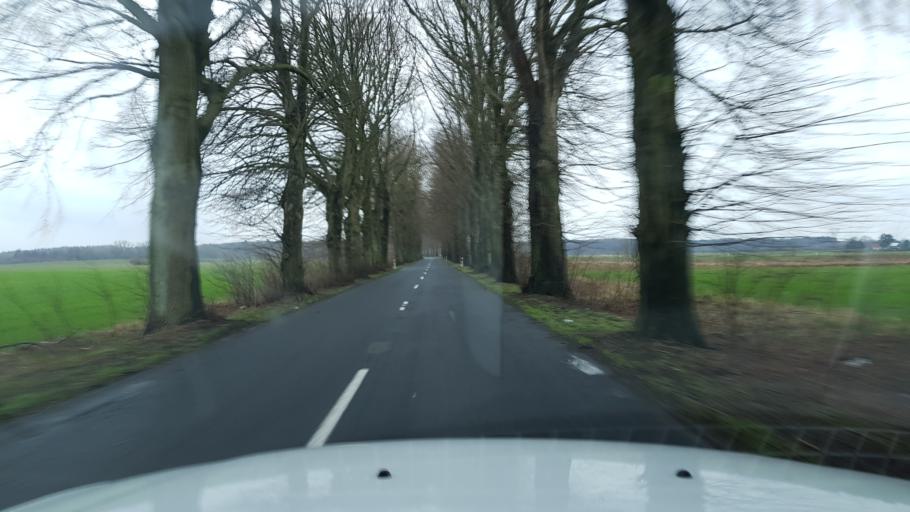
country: PL
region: West Pomeranian Voivodeship
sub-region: Powiat gryficki
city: Brojce
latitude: 54.0587
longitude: 15.3796
